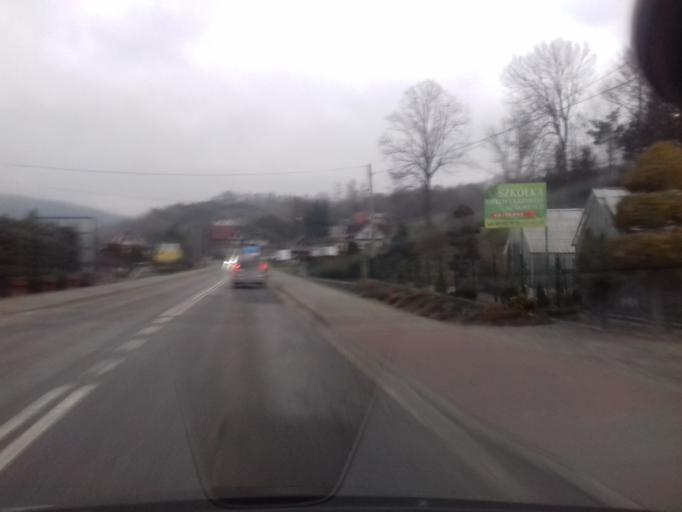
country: PL
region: Lesser Poland Voivodeship
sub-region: Powiat limanowski
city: Mszana Dolna
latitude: 49.6956
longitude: 20.0419
